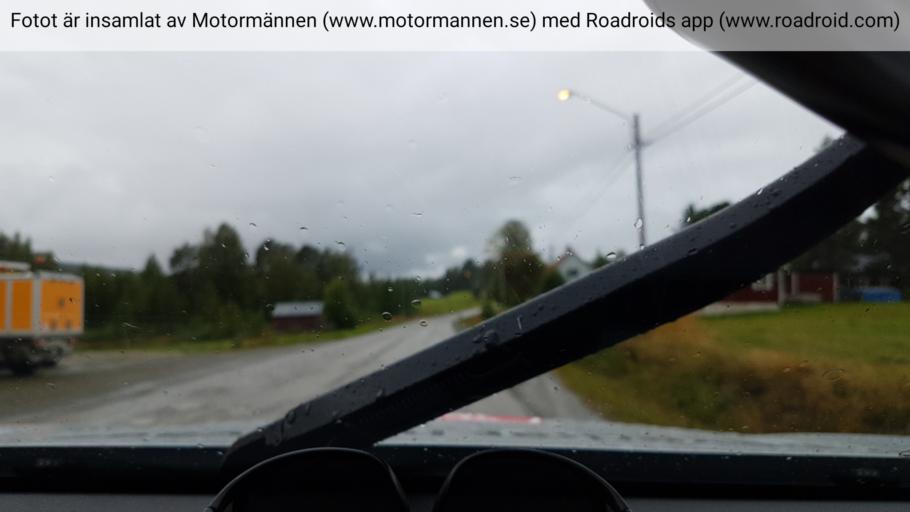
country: SE
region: Vaesterbotten
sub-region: Lycksele Kommun
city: Soderfors
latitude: 64.9666
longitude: 17.6101
